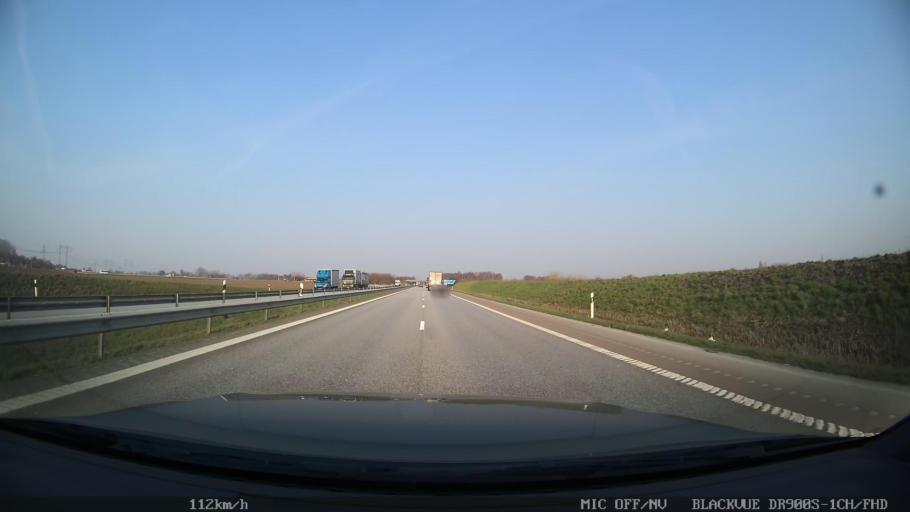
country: SE
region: Skane
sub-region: Kavlinge Kommun
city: Loddekopinge
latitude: 55.7433
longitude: 13.0368
